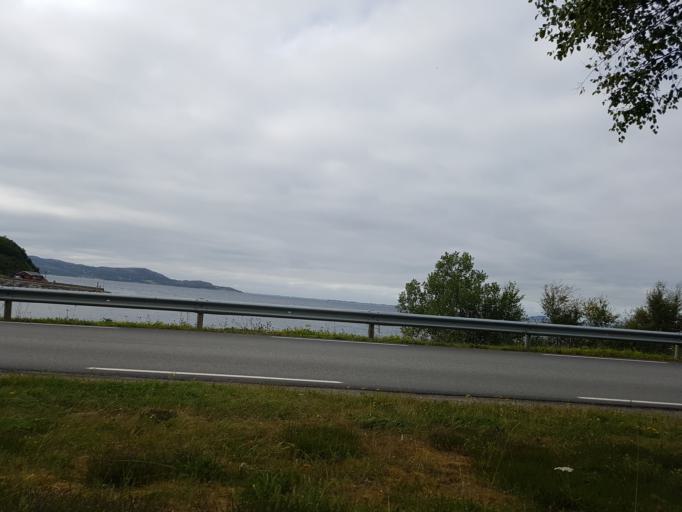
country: NO
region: Sor-Trondelag
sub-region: Agdenes
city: Lensvik
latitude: 63.6341
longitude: 9.8313
